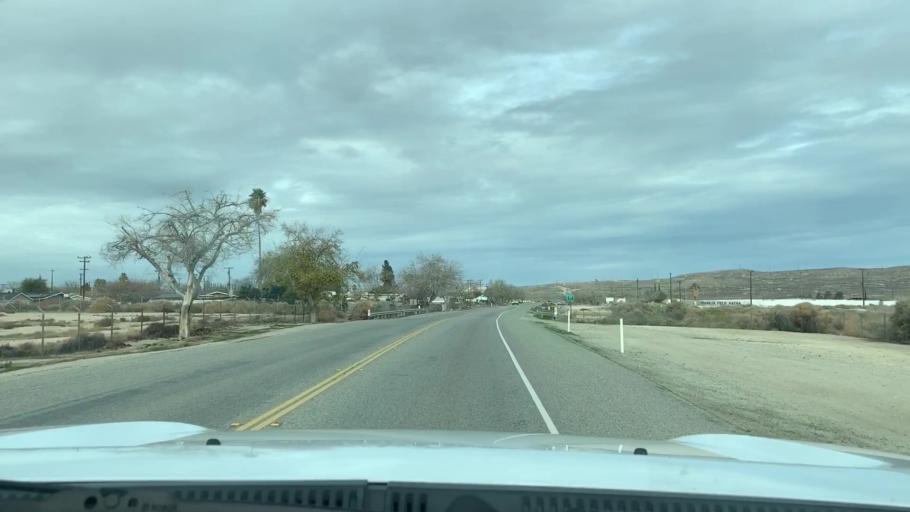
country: US
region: California
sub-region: Kern County
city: Ford City
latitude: 35.1492
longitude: -119.4477
